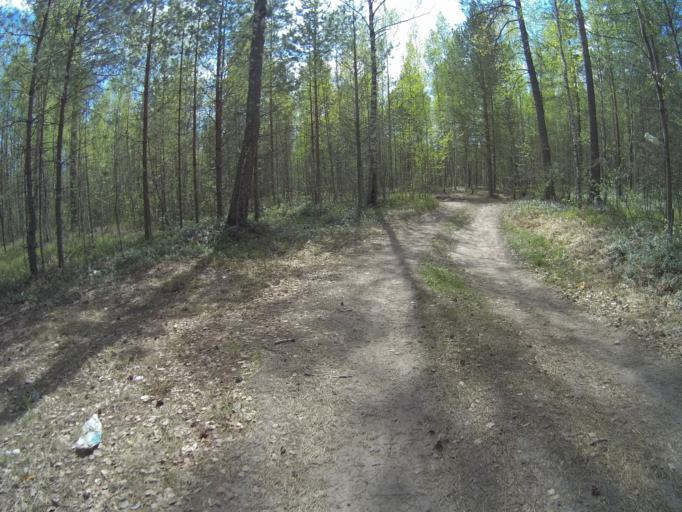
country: RU
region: Vladimir
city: Vorsha
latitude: 55.9511
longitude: 40.1957
